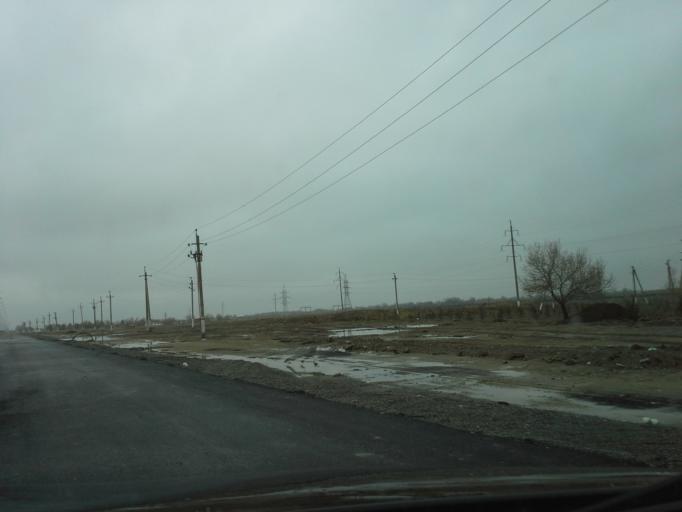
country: TM
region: Ahal
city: Ashgabat
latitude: 37.9658
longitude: 58.4133
